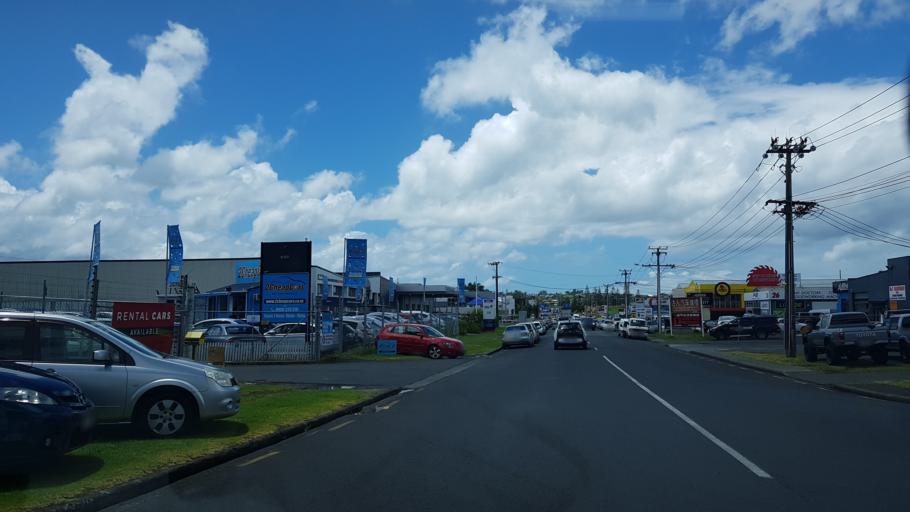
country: NZ
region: Auckland
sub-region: Auckland
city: North Shore
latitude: -36.7747
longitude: 174.7381
